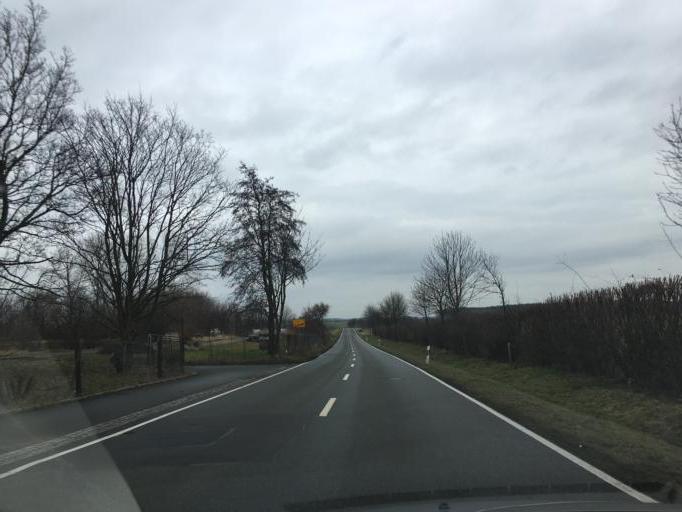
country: DE
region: Saxony
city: Pfaffroda
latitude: 50.8629
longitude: 12.5189
